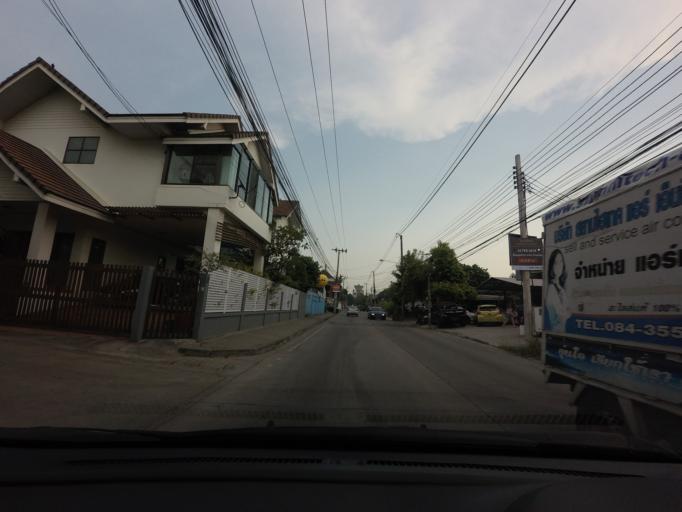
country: TH
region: Bangkok
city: Bang Kapi
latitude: 13.7504
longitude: 100.6270
